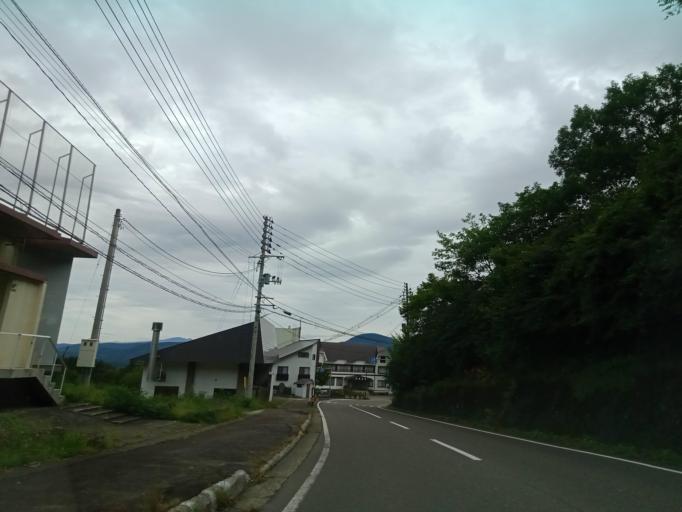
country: JP
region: Niigata
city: Arai
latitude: 36.8878
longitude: 138.1769
